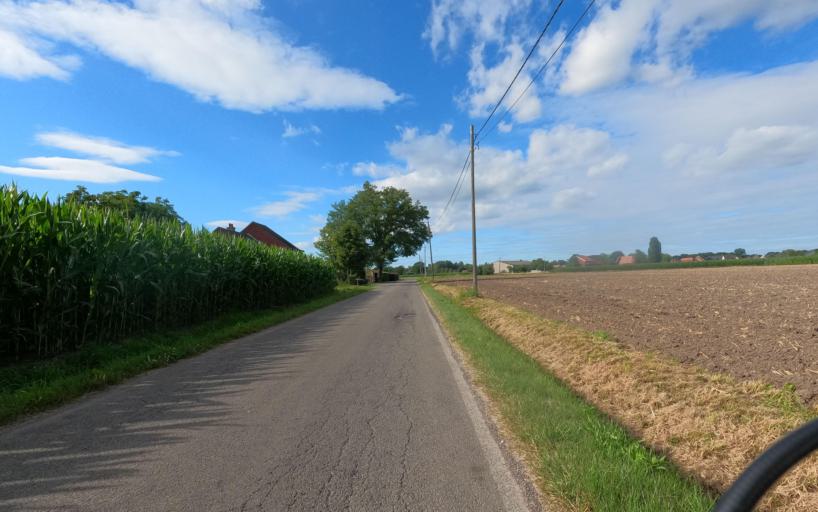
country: BE
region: Flanders
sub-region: Provincie Antwerpen
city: Heist-op-den-Berg
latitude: 51.0346
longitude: 4.7254
